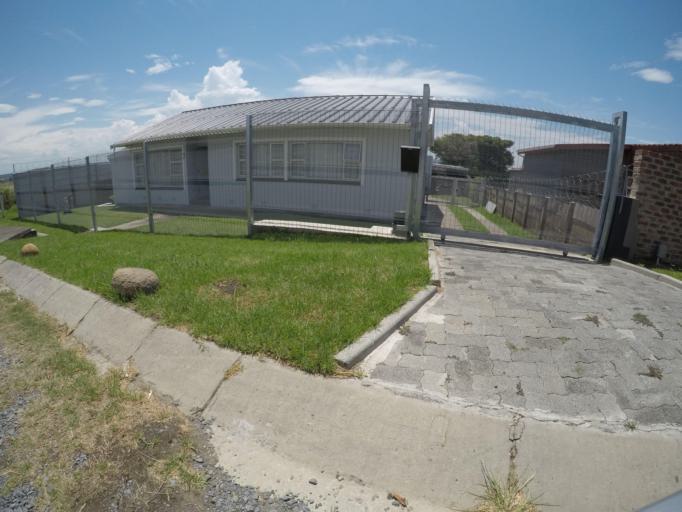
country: ZA
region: Eastern Cape
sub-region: Buffalo City Metropolitan Municipality
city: East London
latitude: -33.0344
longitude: 27.8502
